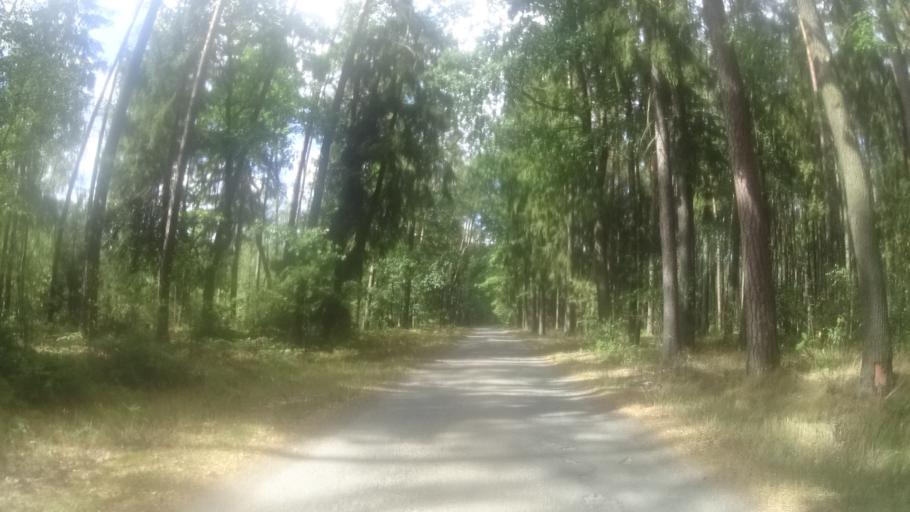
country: CZ
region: Pardubicky
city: Horni Jeleni
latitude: 50.0517
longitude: 16.1540
